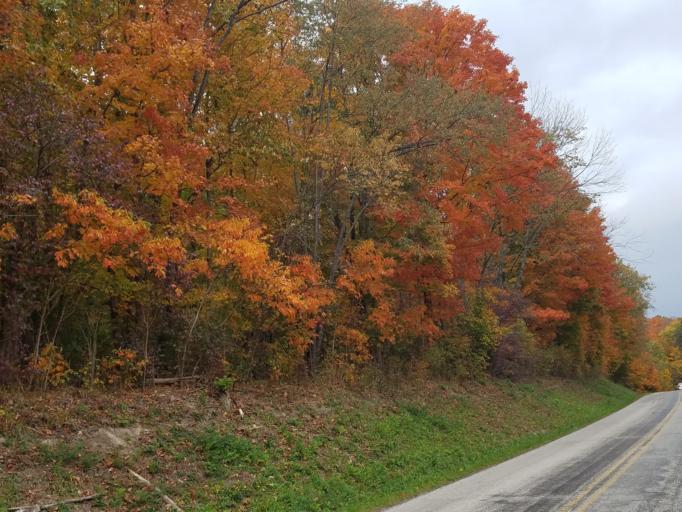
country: US
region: Ohio
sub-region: Sandusky County
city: Bellville
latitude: 40.5700
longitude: -82.4020
